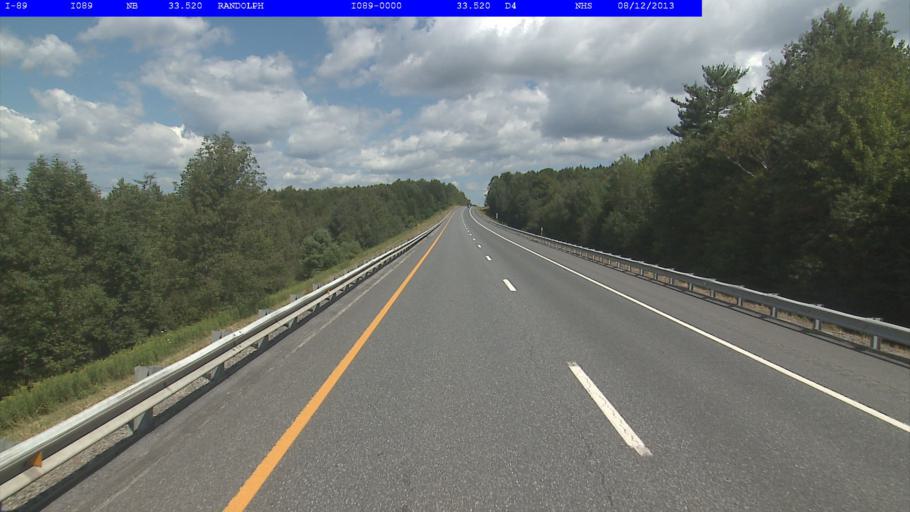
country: US
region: Vermont
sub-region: Orange County
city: Randolph
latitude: 43.9821
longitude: -72.6256
